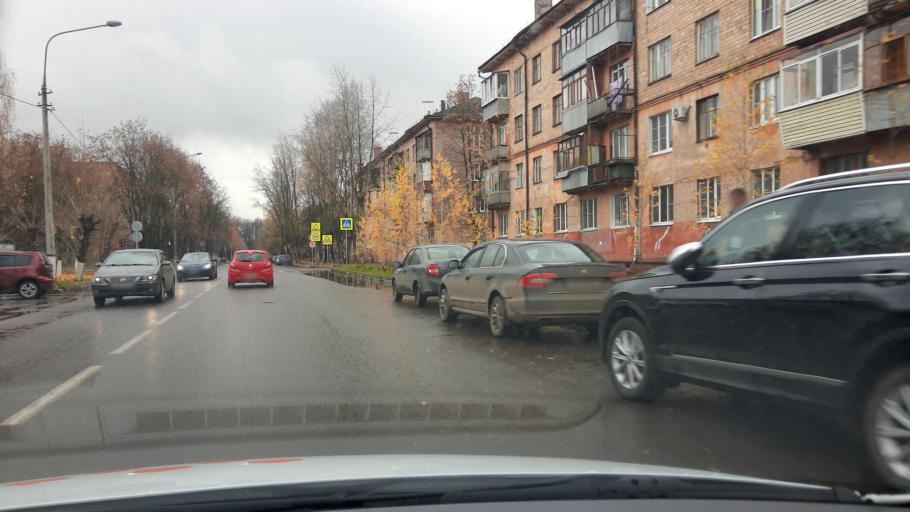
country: RU
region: Moskovskaya
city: Elektrostal'
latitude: 55.7893
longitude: 38.4474
